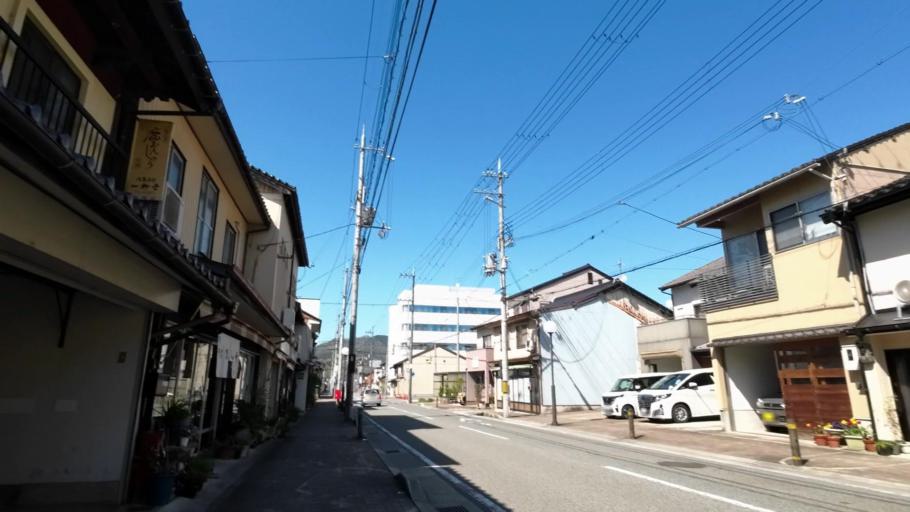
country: JP
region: Hyogo
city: Toyooka
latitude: 35.5464
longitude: 134.8241
